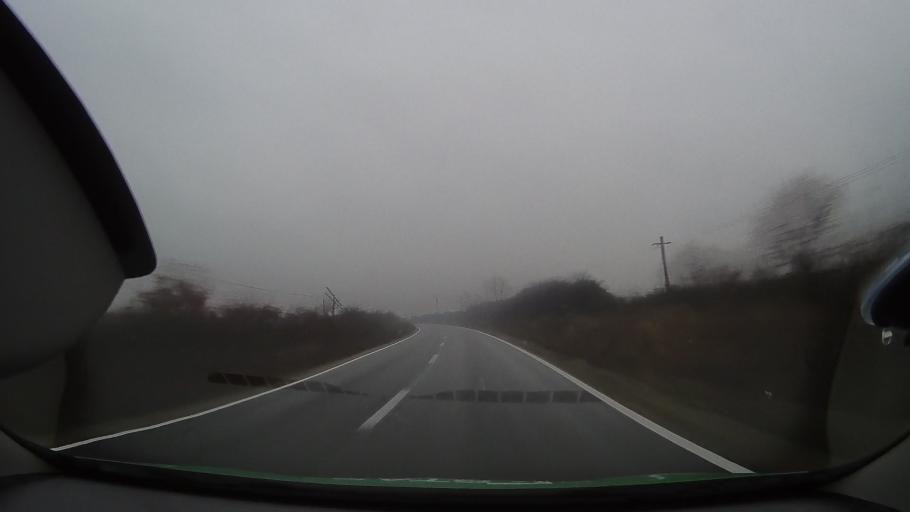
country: RO
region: Bihor
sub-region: Comuna Tinca
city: Tinca
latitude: 46.7285
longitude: 21.9434
